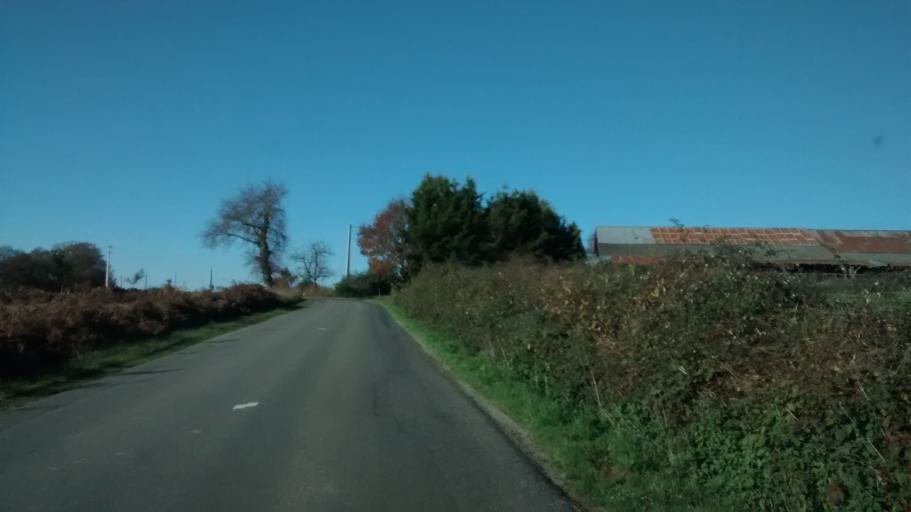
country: FR
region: Brittany
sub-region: Departement d'Ille-et-Vilaine
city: La Bouexiere
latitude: 48.1977
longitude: -1.4489
